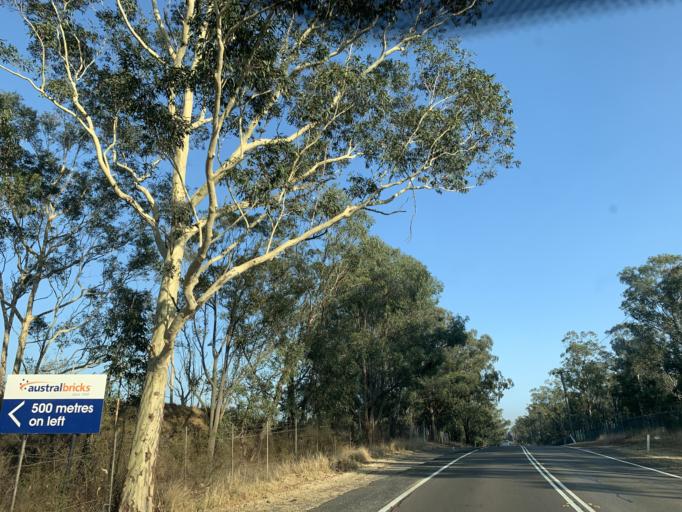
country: AU
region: New South Wales
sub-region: Fairfield
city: Horsley Park
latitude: -33.8296
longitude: 150.8729
